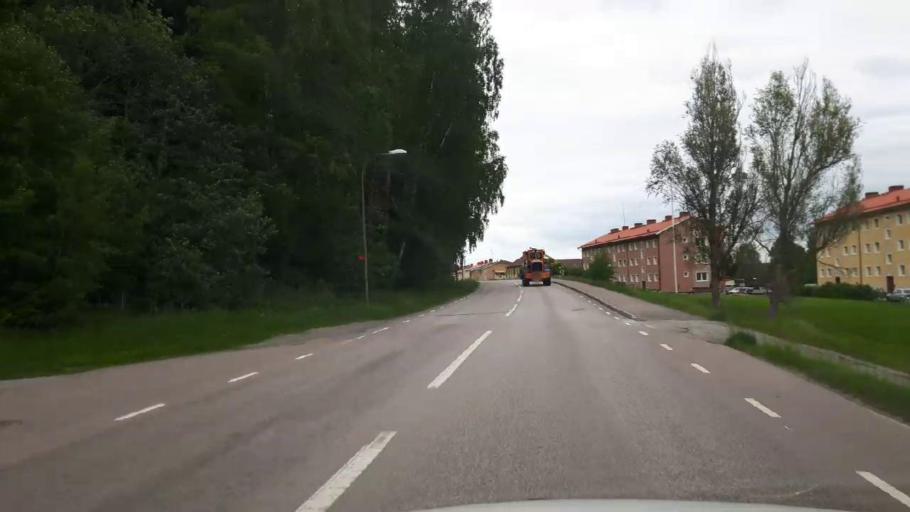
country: SE
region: Vaestmanland
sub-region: Kopings Kommun
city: Kolsva
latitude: 59.6045
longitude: 15.8343
